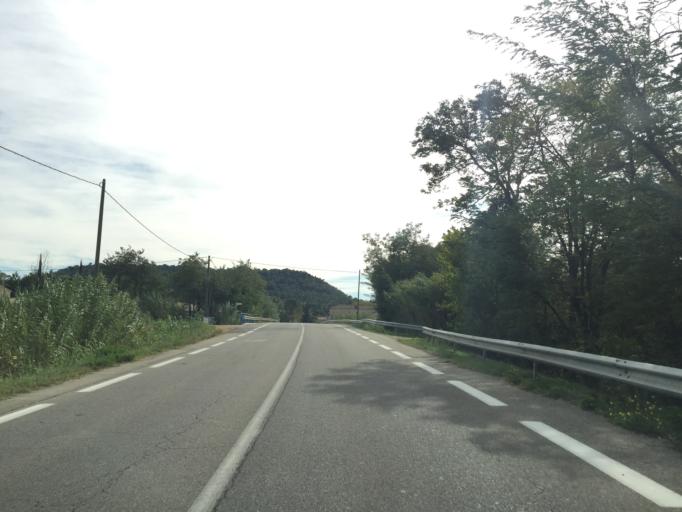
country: FR
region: Provence-Alpes-Cote d'Azur
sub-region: Departement du Vaucluse
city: Mondragon
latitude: 44.2514
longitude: 4.7316
